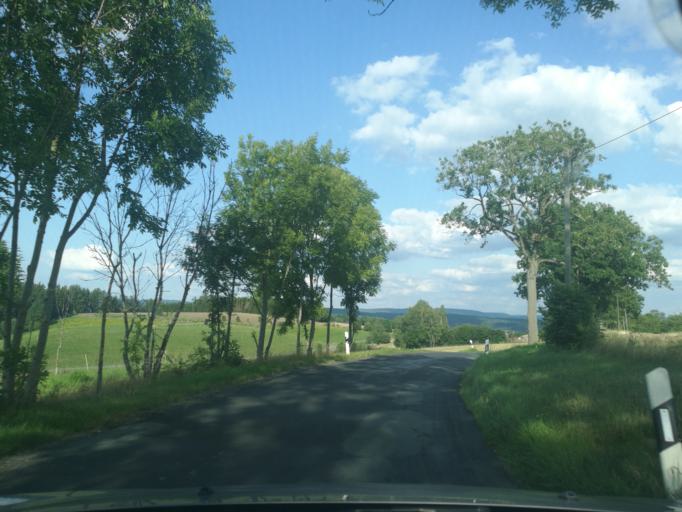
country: DE
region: Saxony
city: Adorf
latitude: 50.3162
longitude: 12.2333
